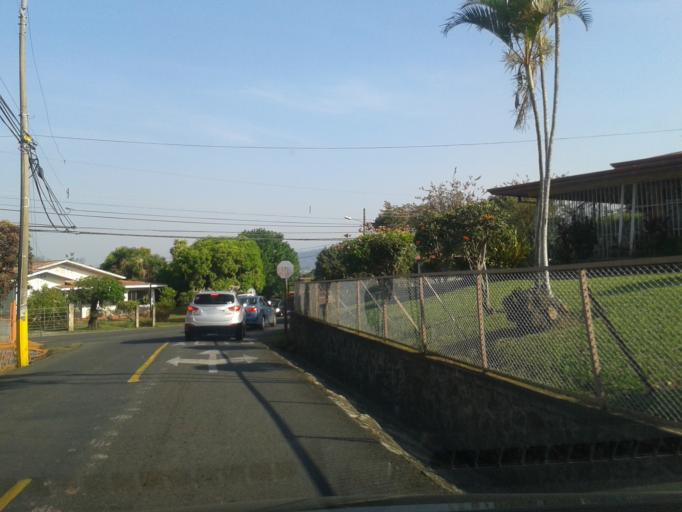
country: CR
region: Heredia
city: Mercedes
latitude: 10.0112
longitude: -84.1475
